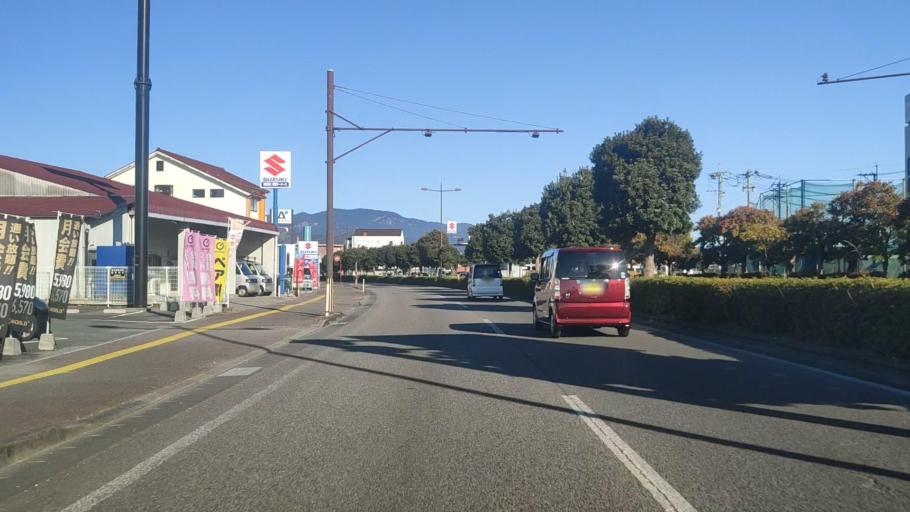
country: JP
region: Miyazaki
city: Nobeoka
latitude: 32.5772
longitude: 131.6835
